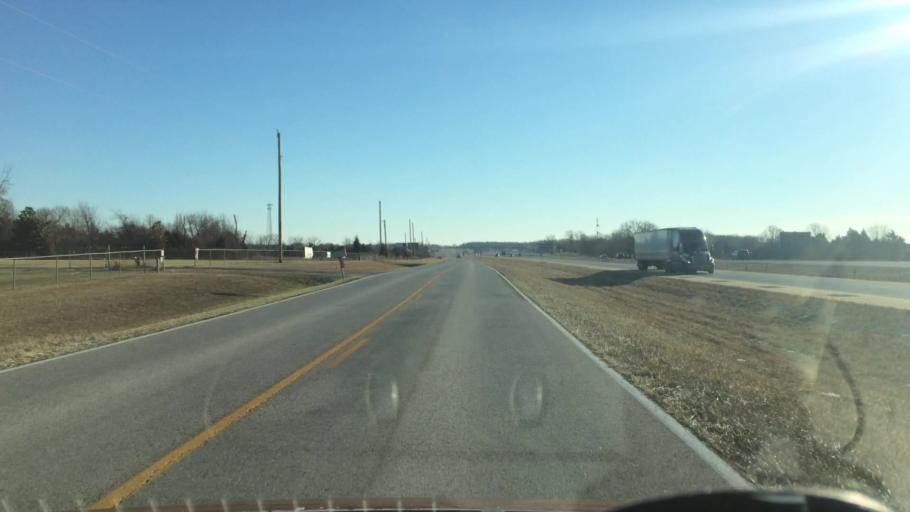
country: US
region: Missouri
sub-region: Greene County
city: Strafford
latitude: 37.2710
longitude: -93.0966
